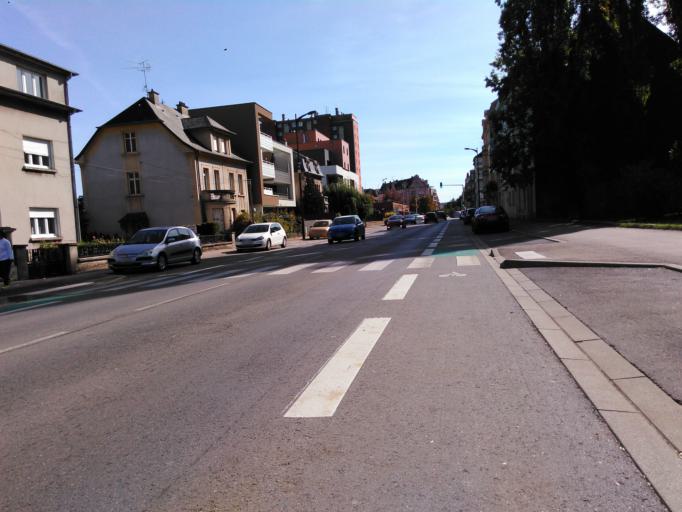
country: FR
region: Lorraine
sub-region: Departement de la Moselle
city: Thionville
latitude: 49.3645
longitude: 6.1688
